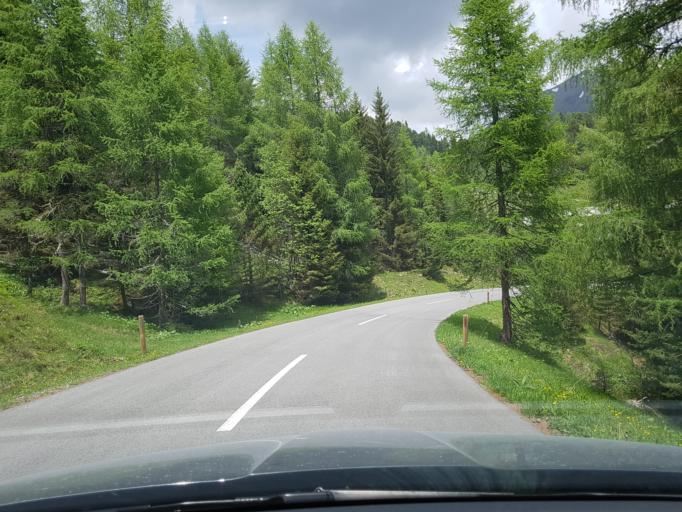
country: AT
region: Carinthia
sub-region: Politischer Bezirk Spittal an der Drau
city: Kleinkirchheim
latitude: 46.8962
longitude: 13.8133
